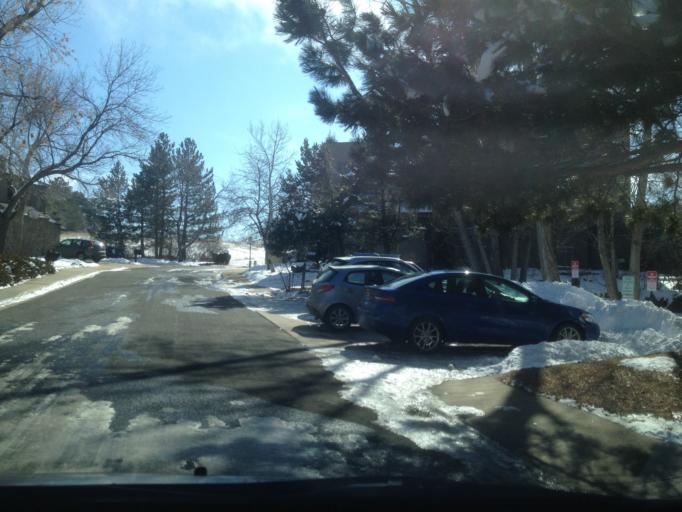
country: US
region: Colorado
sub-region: Boulder County
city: Boulder
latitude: 40.0472
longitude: -105.2906
